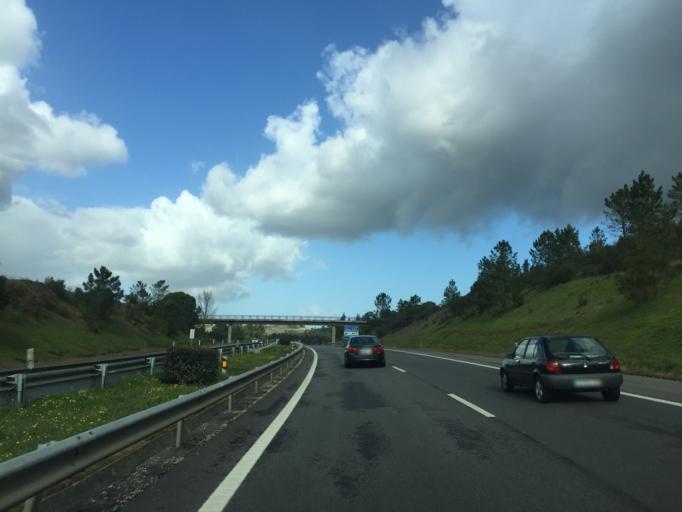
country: PT
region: Lisbon
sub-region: Mafra
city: Venda do Pinheiro
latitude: 38.9295
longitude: -9.2173
